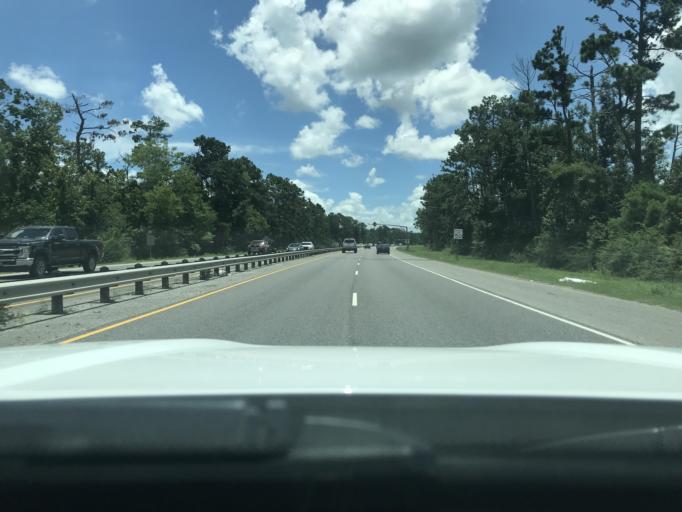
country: US
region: Louisiana
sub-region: Calcasieu Parish
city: Moss Bluff
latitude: 30.2813
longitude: -93.1855
